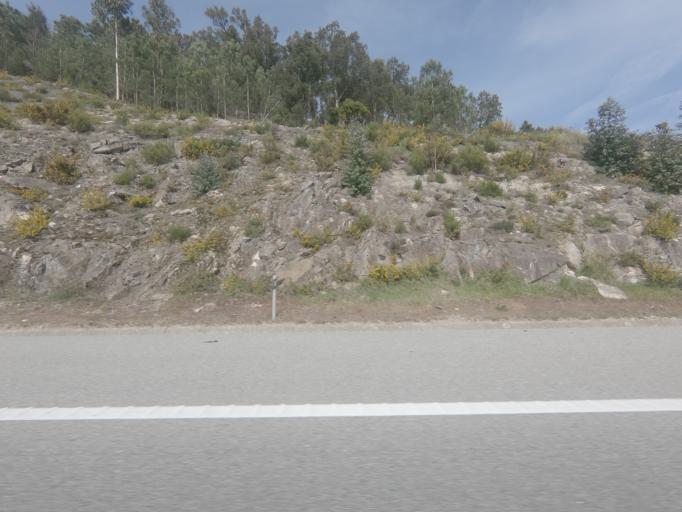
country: PT
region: Aveiro
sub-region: Sever do Vouga
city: Sever do Vouga
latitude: 40.6699
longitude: -8.3317
